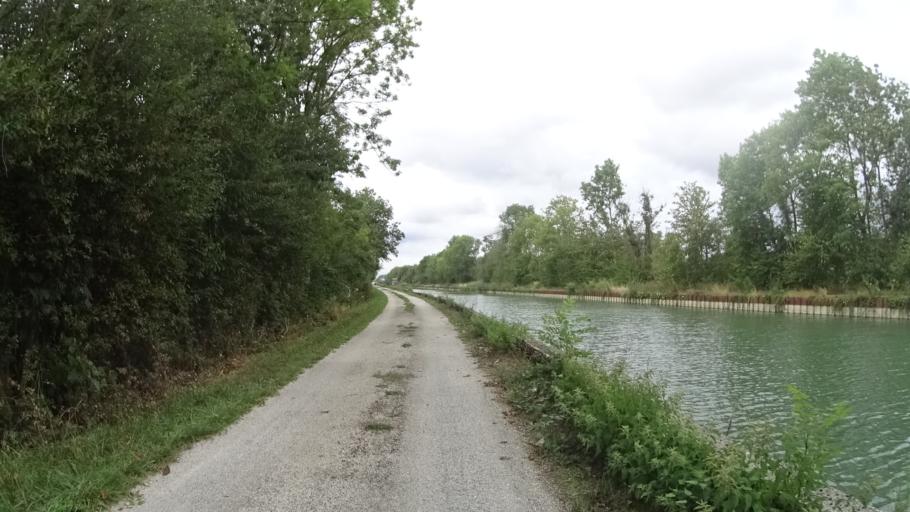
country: FR
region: Picardie
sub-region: Departement de l'Aisne
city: La Fere
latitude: 49.6961
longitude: 3.3707
